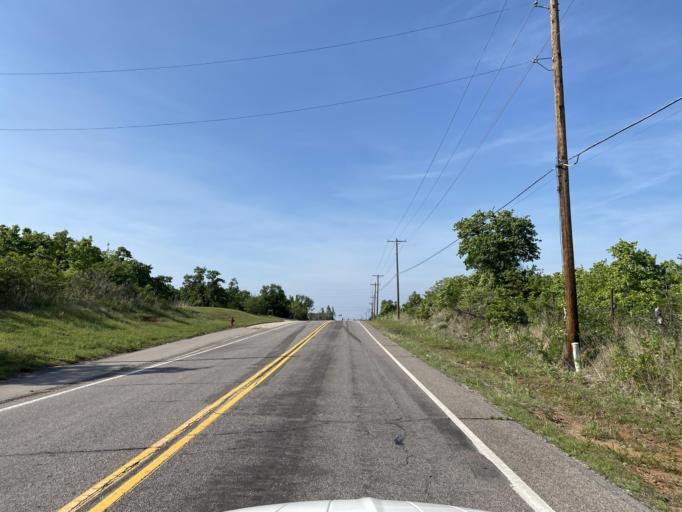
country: US
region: Oklahoma
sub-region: Oklahoma County
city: Nicoma Park
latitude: 35.4469
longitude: -97.3357
